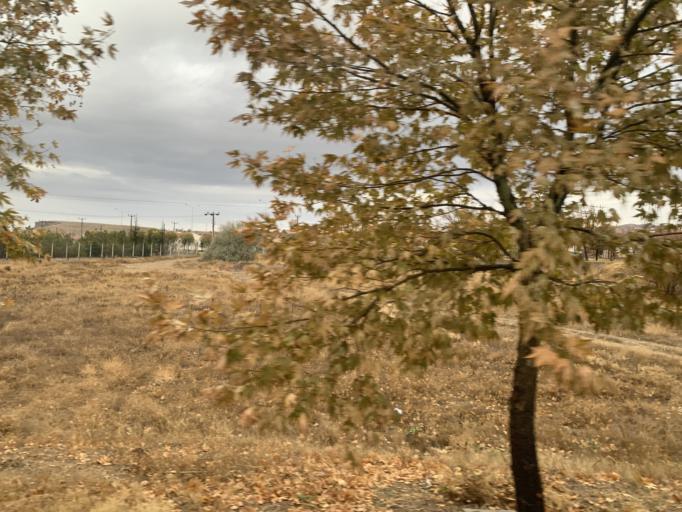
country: TR
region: Nevsehir
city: Avanos
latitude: 38.7212
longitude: 34.8620
